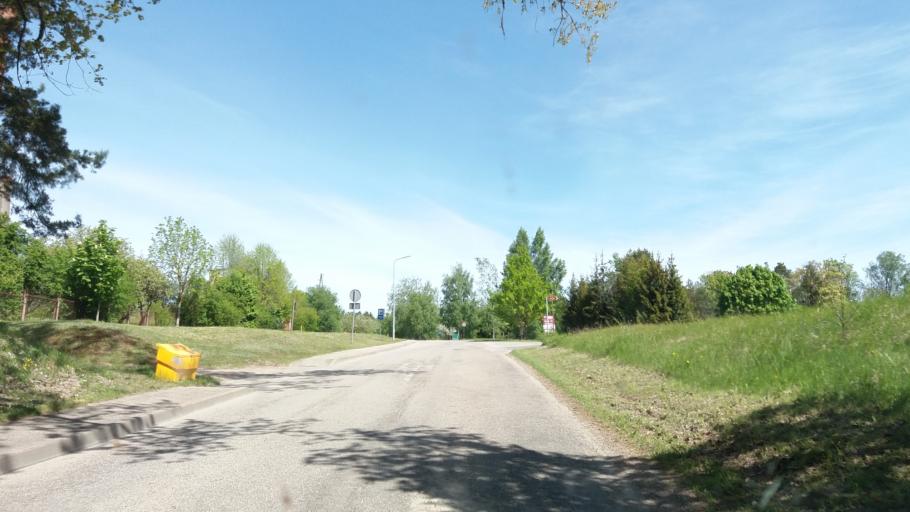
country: LV
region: Talsu Rajons
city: Sabile
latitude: 57.0502
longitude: 22.5776
